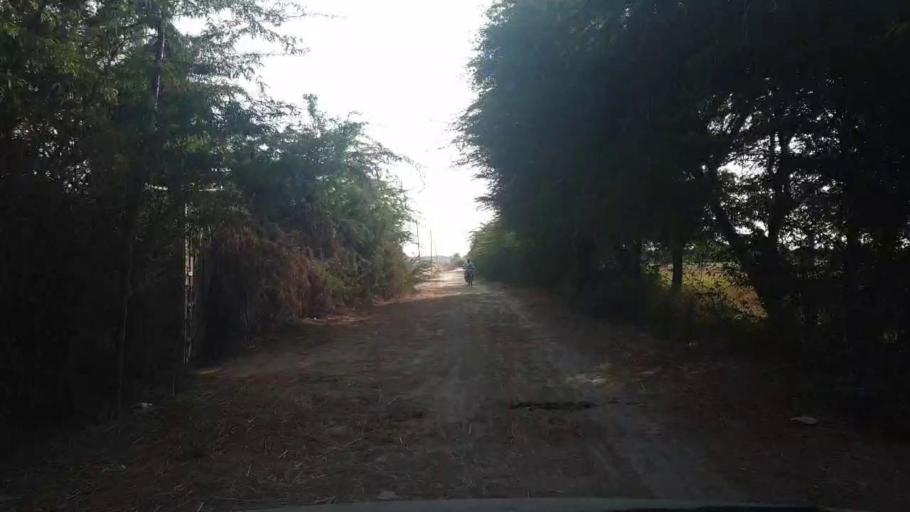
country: PK
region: Sindh
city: Badin
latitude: 24.6439
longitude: 68.8032
